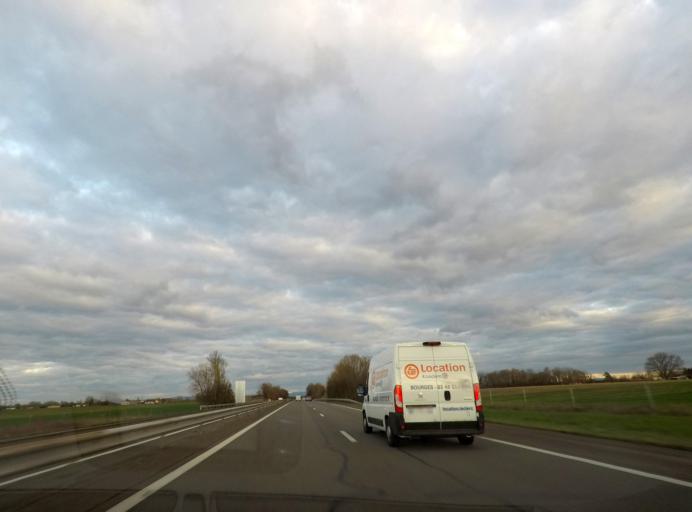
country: FR
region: Rhone-Alpes
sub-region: Departement de l'Ain
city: Saint-Cyr-sur-Menthon
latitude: 46.2821
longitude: 4.9613
